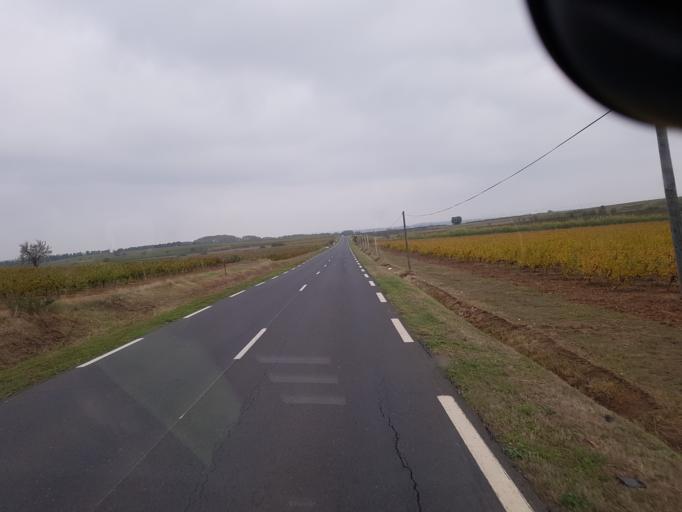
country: FR
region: Languedoc-Roussillon
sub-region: Departement de l'Herault
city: Pinet
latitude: 43.3936
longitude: 3.5382
